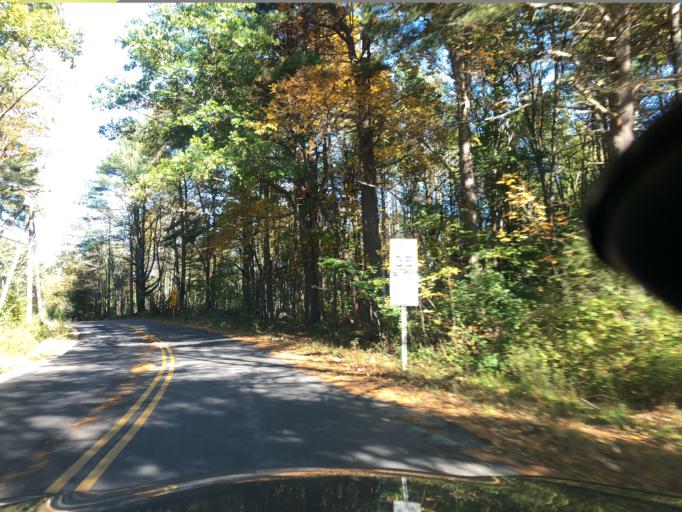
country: US
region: New Hampshire
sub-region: Rockingham County
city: Newmarket
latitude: 43.0883
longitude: -70.9469
